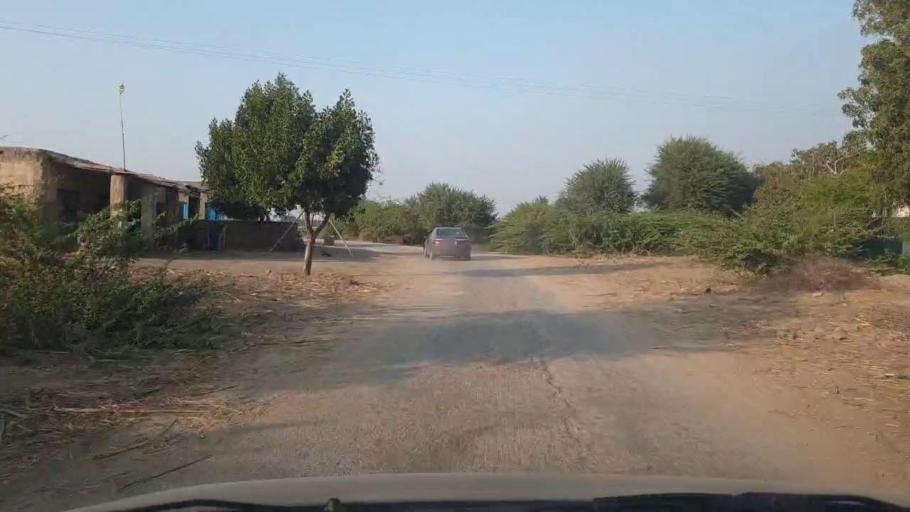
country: PK
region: Sindh
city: Mirwah Gorchani
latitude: 25.3673
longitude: 69.1778
